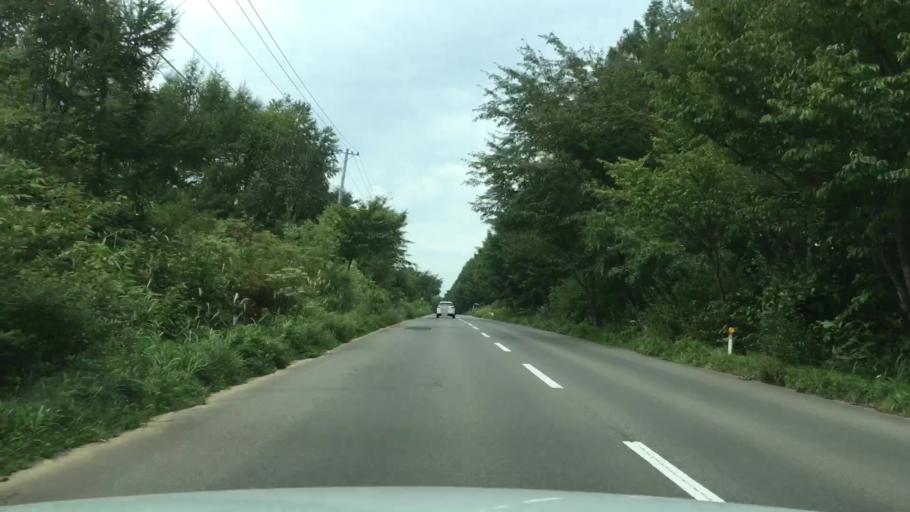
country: JP
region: Aomori
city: Shimokizukuri
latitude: 40.7136
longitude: 140.3228
